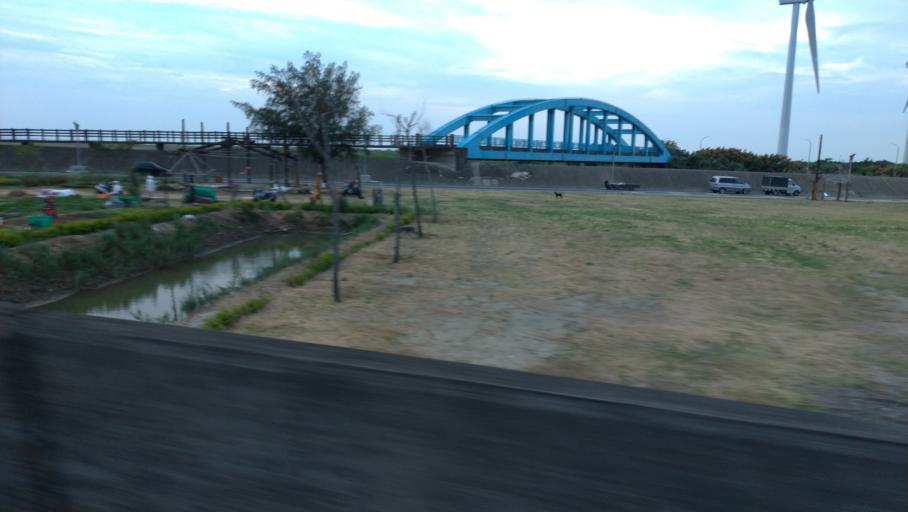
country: TW
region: Taiwan
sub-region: Hsinchu
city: Hsinchu
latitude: 24.7600
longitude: 120.9070
